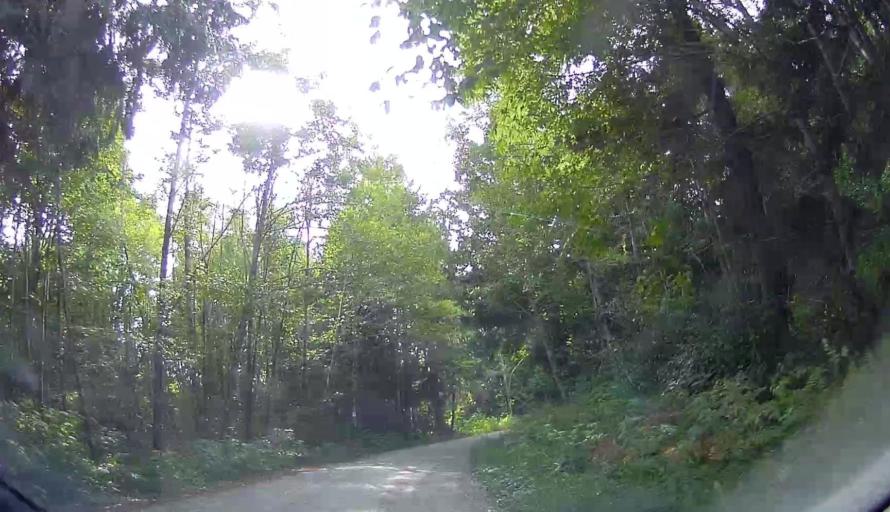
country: US
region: Washington
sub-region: Skagit County
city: Burlington
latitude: 48.5874
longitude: -122.3868
